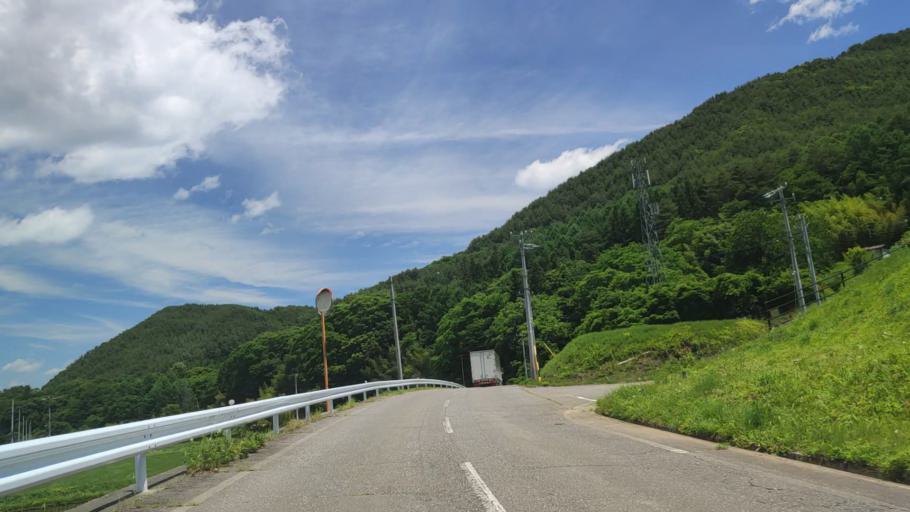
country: JP
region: Nagano
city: Kamimaruko
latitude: 36.2287
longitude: 138.2539
